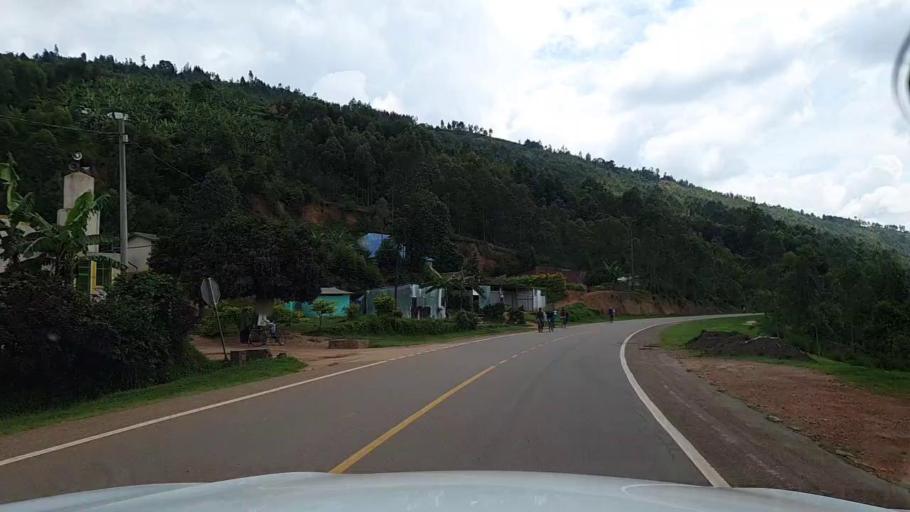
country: RW
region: Kigali
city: Kigali
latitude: -1.8115
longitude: 30.0988
